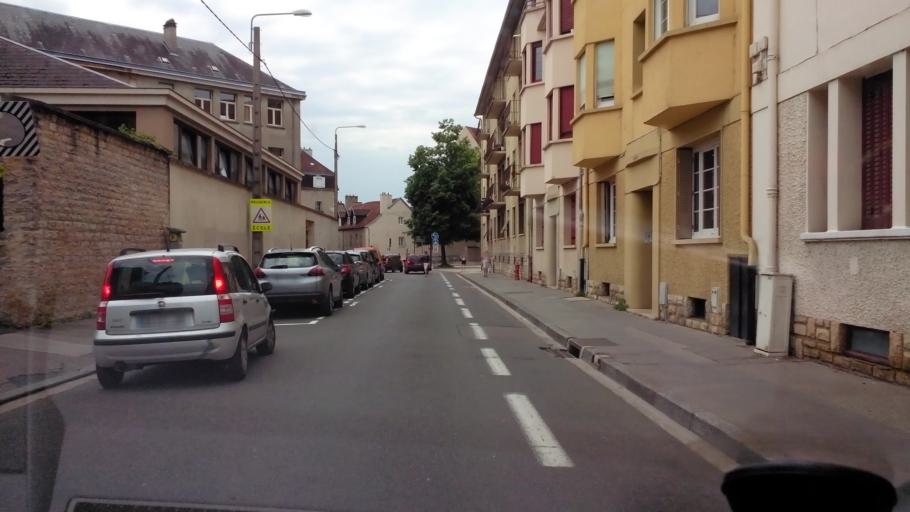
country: FR
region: Bourgogne
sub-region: Departement de la Cote-d'Or
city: Dijon
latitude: 47.3265
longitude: 5.0409
